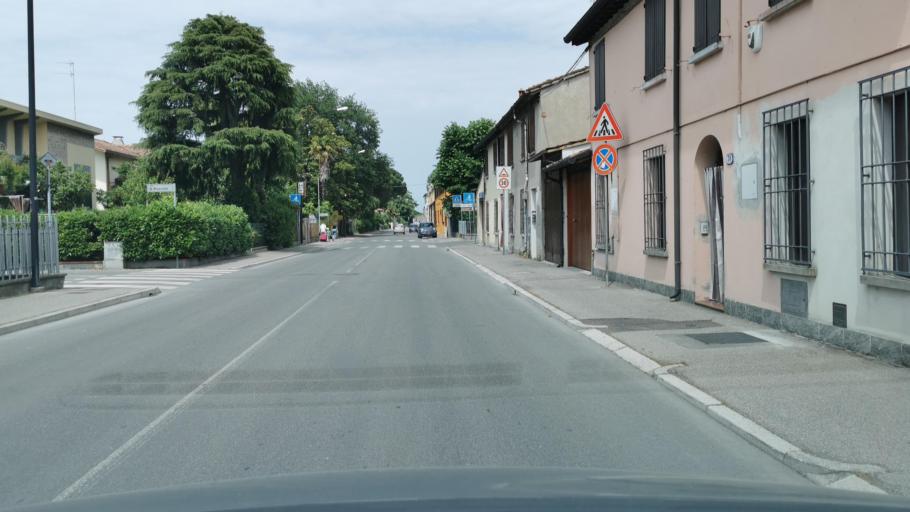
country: IT
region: Emilia-Romagna
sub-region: Provincia di Ravenna
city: Bagnacavallo
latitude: 44.4162
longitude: 11.9725
